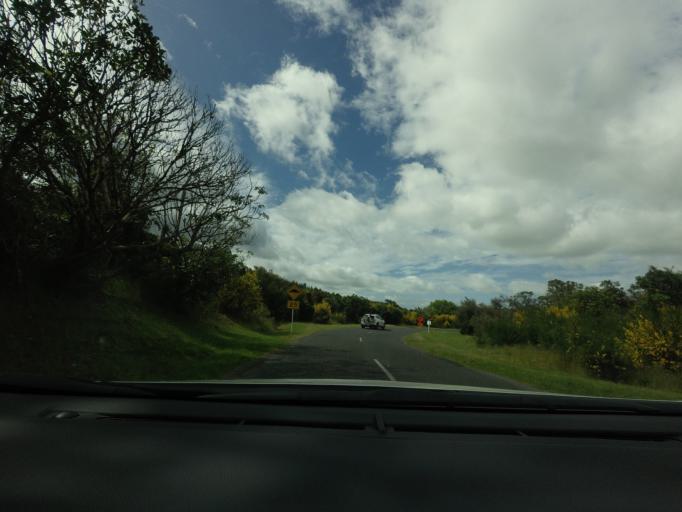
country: NZ
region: Bay of Plenty
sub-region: Rotorua District
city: Rotorua
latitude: -38.3527
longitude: 176.3684
